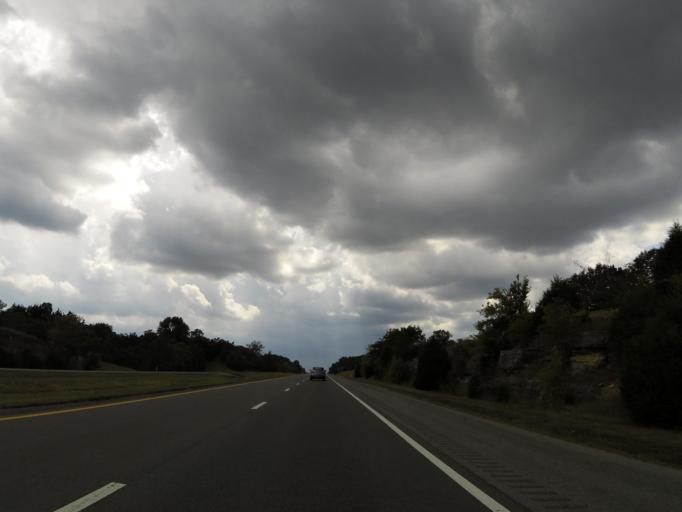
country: US
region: Tennessee
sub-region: Wilson County
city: Lebanon
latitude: 36.1460
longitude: -86.3701
